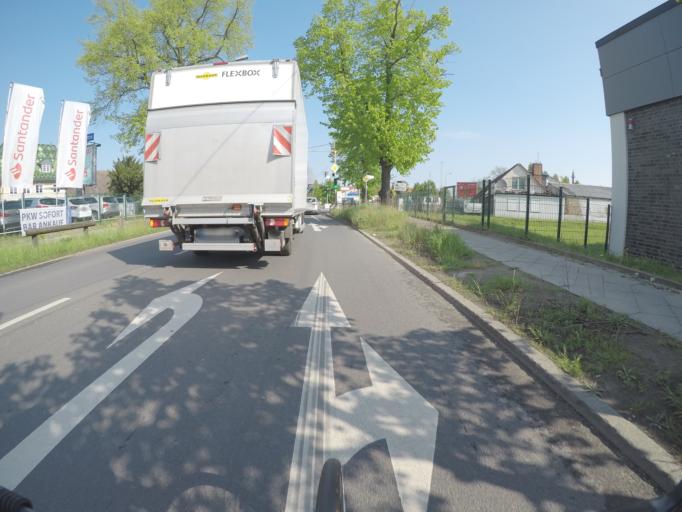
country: DE
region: Berlin
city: Buchholz
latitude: 52.6120
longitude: 13.4339
